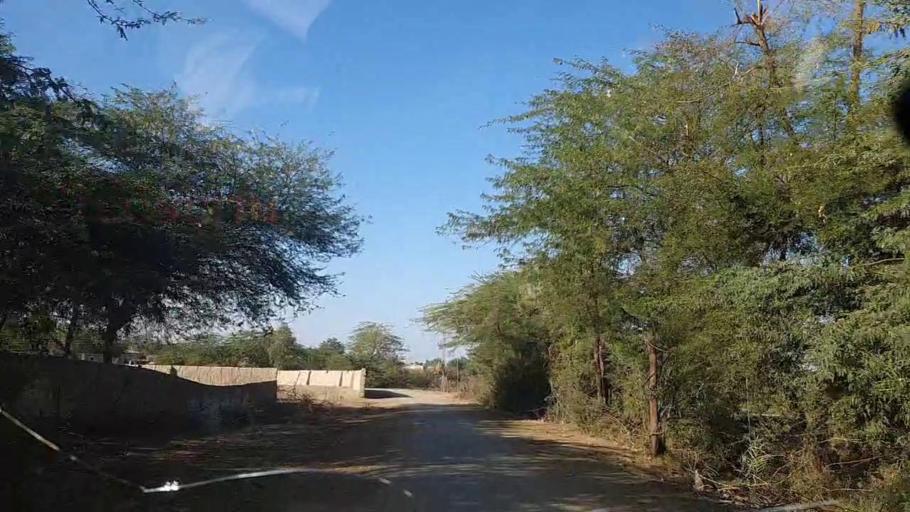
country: PK
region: Sindh
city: Khanpur
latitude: 27.7660
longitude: 69.2945
